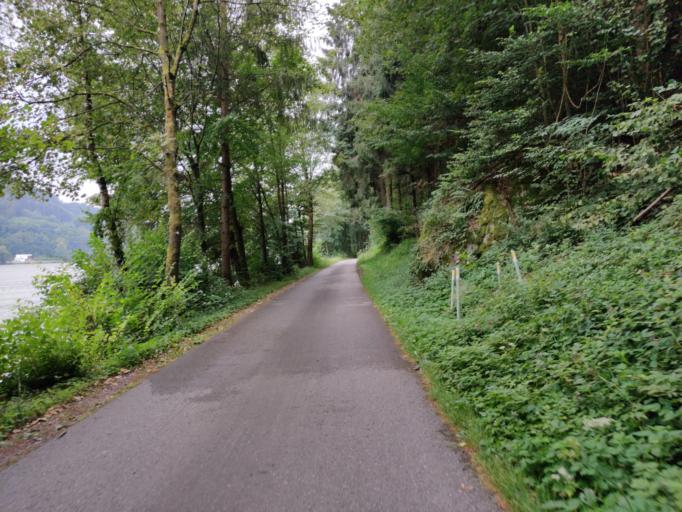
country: AT
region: Lower Austria
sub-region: Politischer Bezirk Melk
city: Nochling
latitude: 48.2172
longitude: 14.9497
